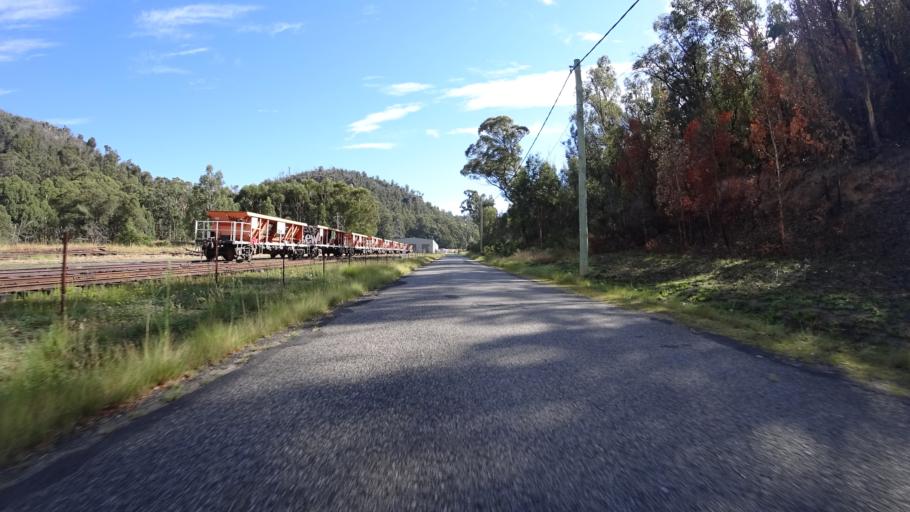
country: AU
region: New South Wales
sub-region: Lithgow
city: Lithgow
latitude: -33.4633
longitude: 150.1690
